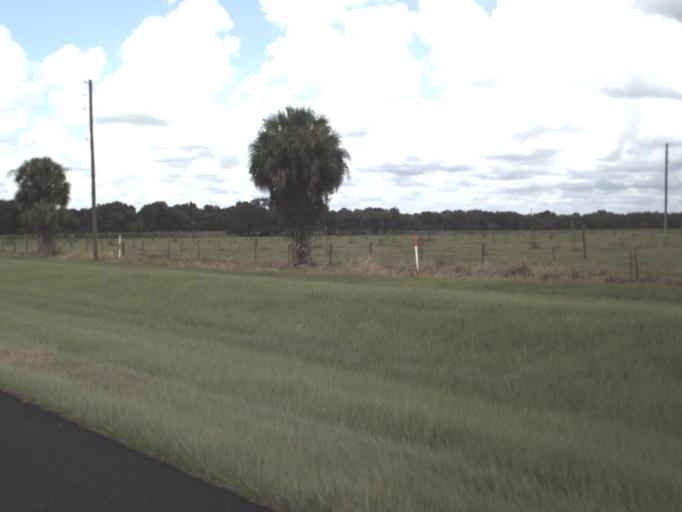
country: US
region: Florida
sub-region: Hardee County
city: Zolfo Springs
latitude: 27.4803
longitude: -81.7974
